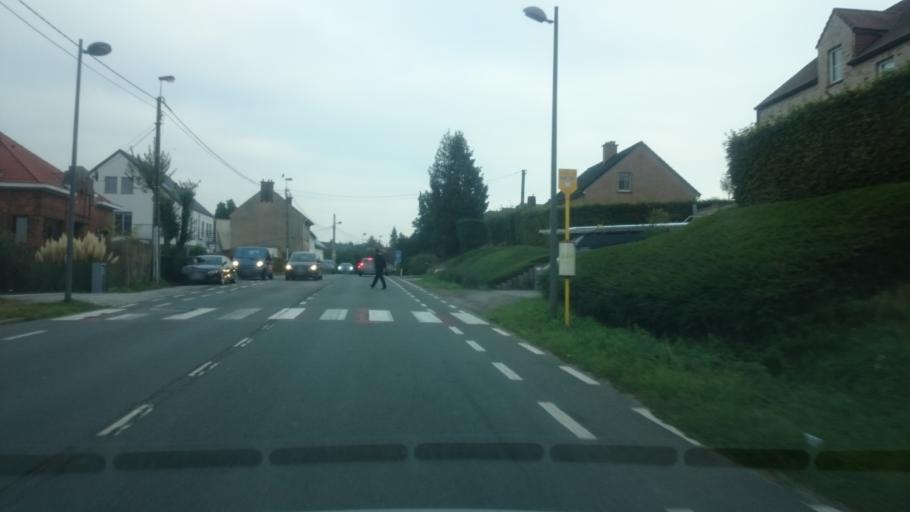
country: BE
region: Wallonia
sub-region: Province du Brabant Wallon
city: Grez-Doiceau
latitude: 50.7417
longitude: 4.6877
